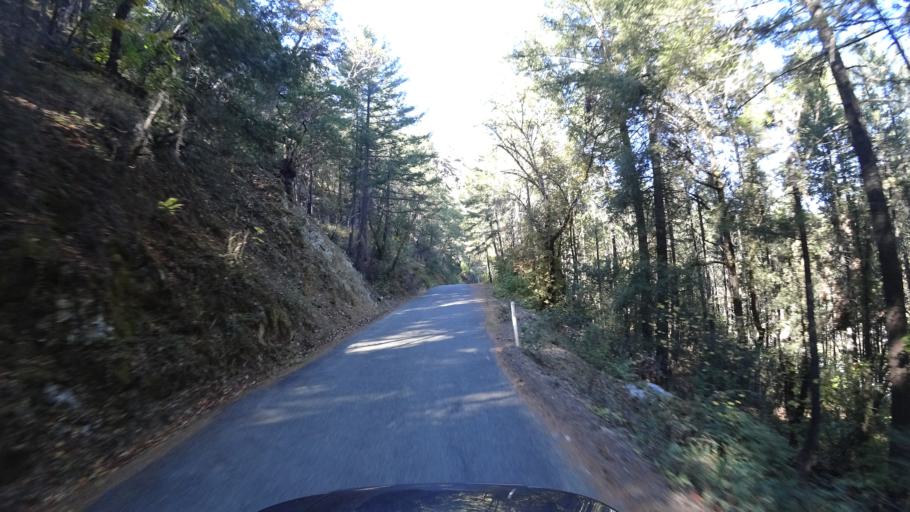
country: US
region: California
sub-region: Humboldt County
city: Willow Creek
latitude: 41.3014
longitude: -123.3692
